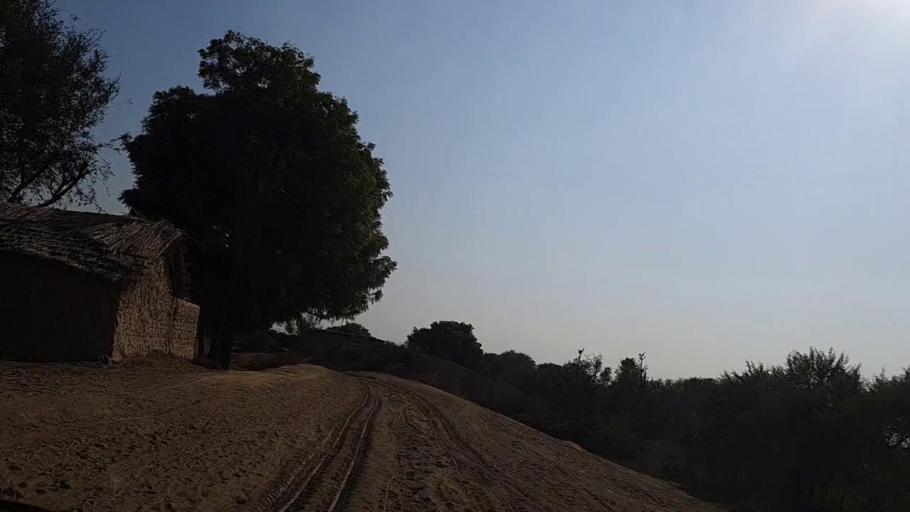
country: PK
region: Sindh
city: Sakrand
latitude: 26.0214
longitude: 68.3098
